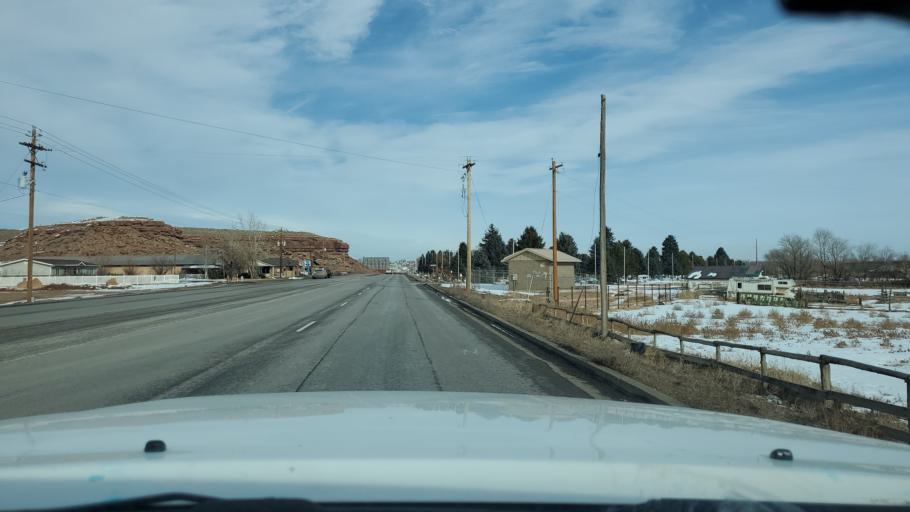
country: US
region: Utah
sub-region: Duchesne County
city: Roosevelt
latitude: 40.2874
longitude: -110.0032
